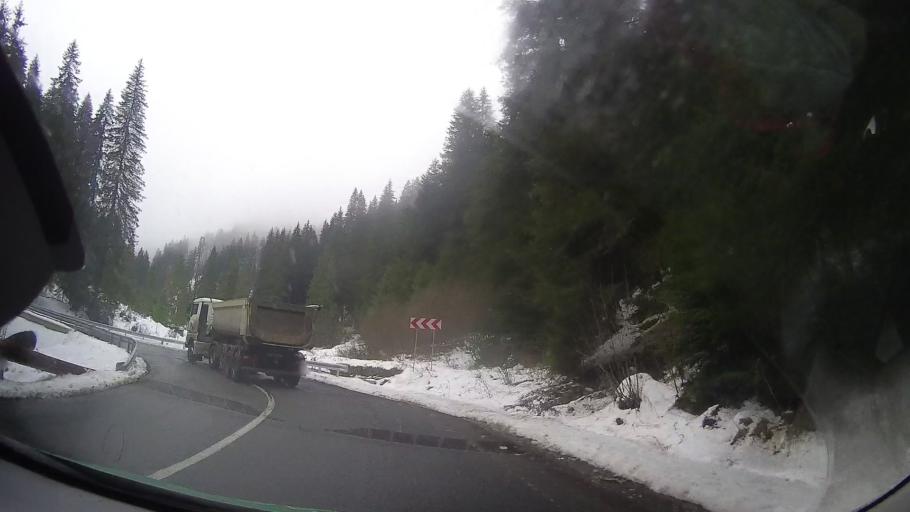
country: RO
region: Neamt
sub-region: Comuna Bicaz Chei
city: Bicaz Chei
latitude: 46.7824
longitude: 25.7489
